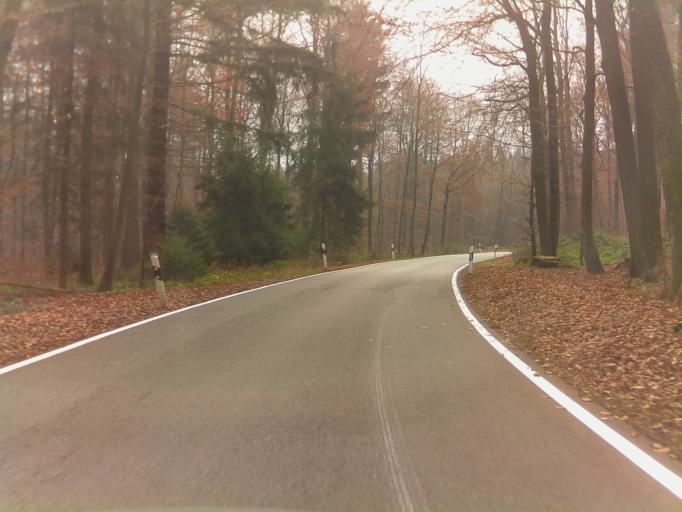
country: DE
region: Baden-Wuerttemberg
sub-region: Karlsruhe Region
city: Heidelberg
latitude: 49.3994
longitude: 8.7288
